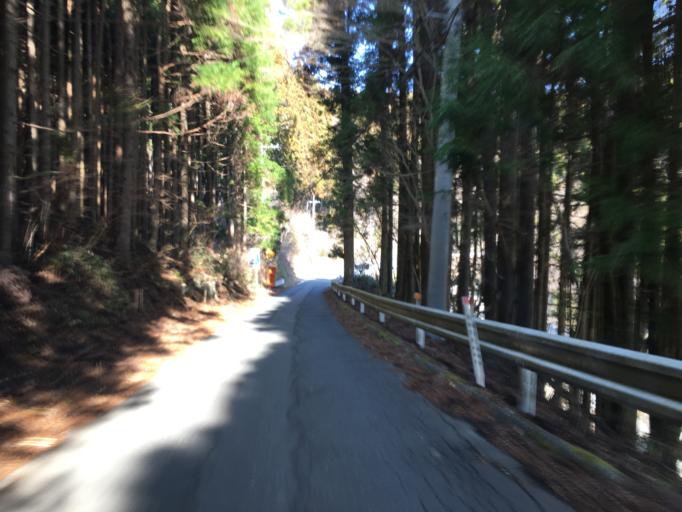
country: JP
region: Ibaraki
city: Takahagi
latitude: 36.8029
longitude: 140.6129
